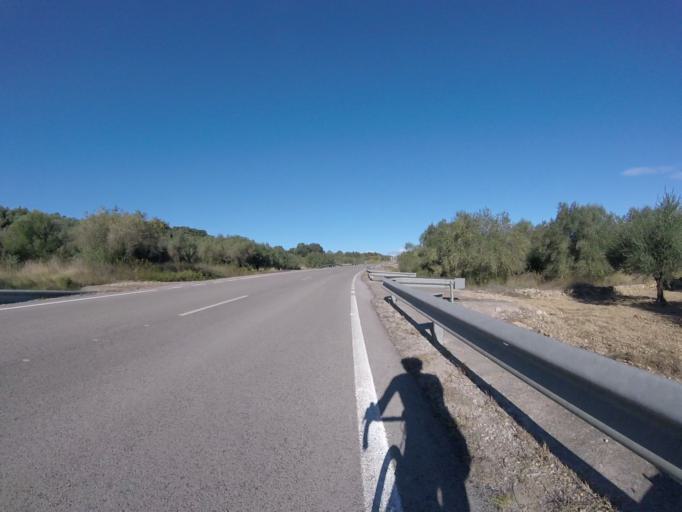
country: ES
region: Valencia
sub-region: Provincia de Castello
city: Cervera del Maestre
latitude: 40.4703
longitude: 0.2428
